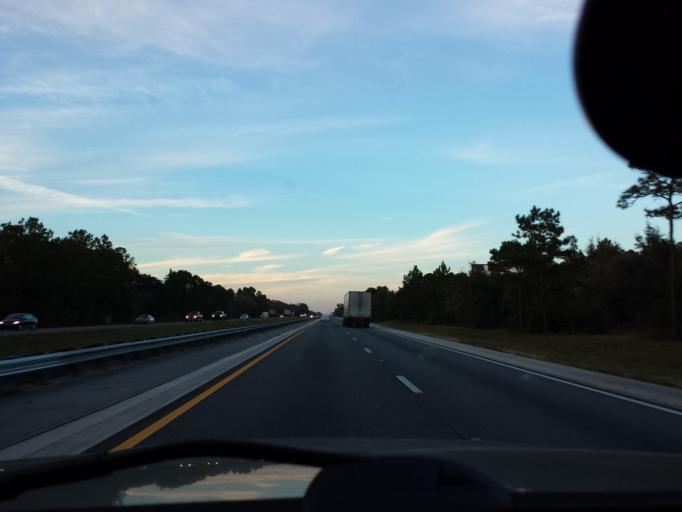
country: US
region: Florida
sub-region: Sumter County
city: Lake Panasoffkee
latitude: 28.7777
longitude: -82.0866
